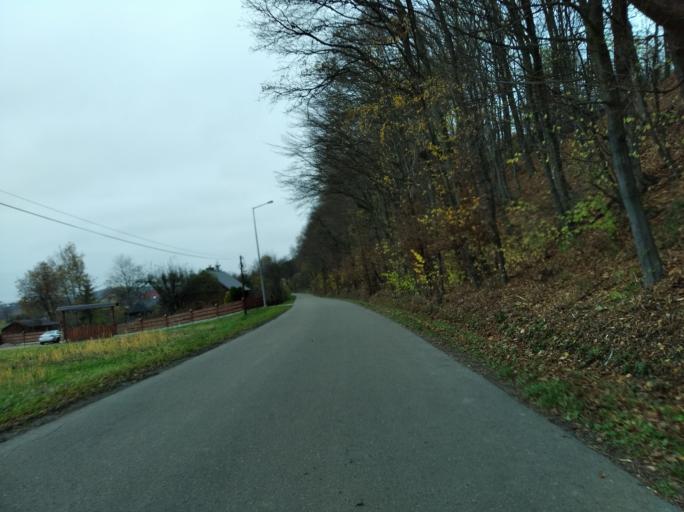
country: PL
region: Subcarpathian Voivodeship
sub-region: Powiat strzyzowski
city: Frysztak
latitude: 49.8313
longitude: 21.6309
